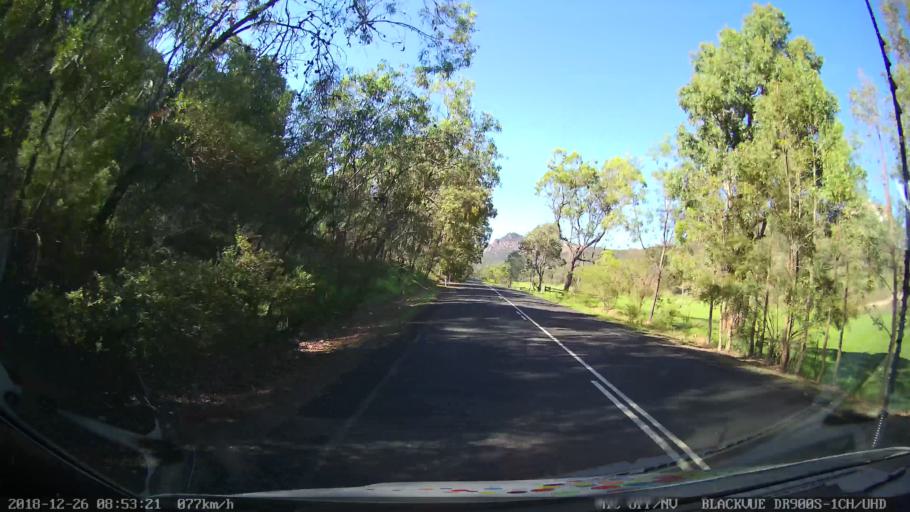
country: AU
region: New South Wales
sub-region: Mid-Western Regional
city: Kandos
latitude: -32.6032
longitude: 150.0780
